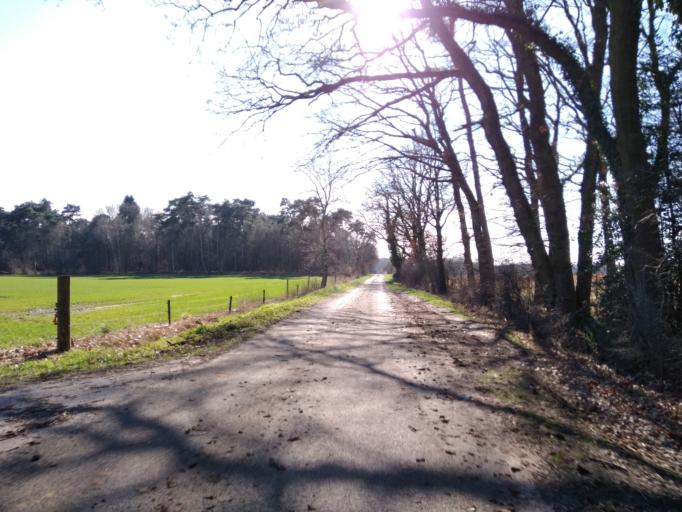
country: DE
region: North Rhine-Westphalia
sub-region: Regierungsbezirk Dusseldorf
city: Schermbeck
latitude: 51.6296
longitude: 6.8411
